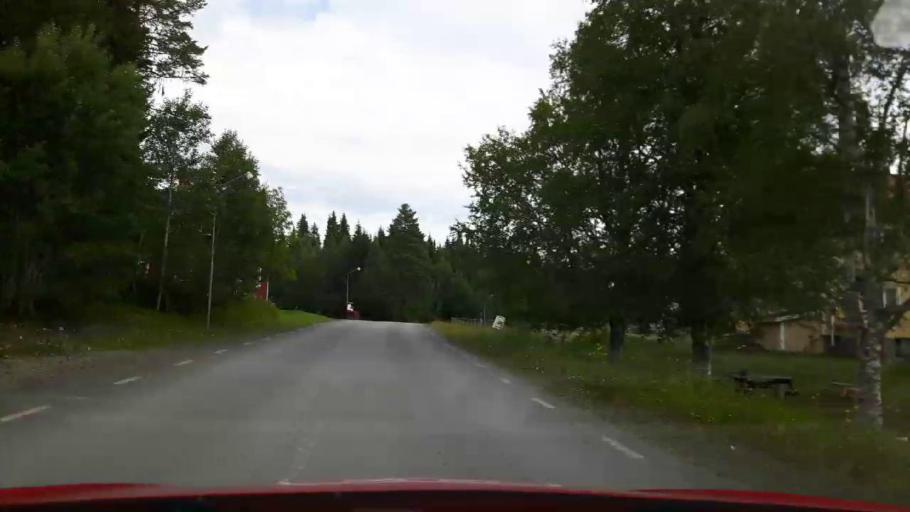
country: SE
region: Jaemtland
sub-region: OEstersunds Kommun
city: Lit
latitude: 63.4179
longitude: 15.2511
